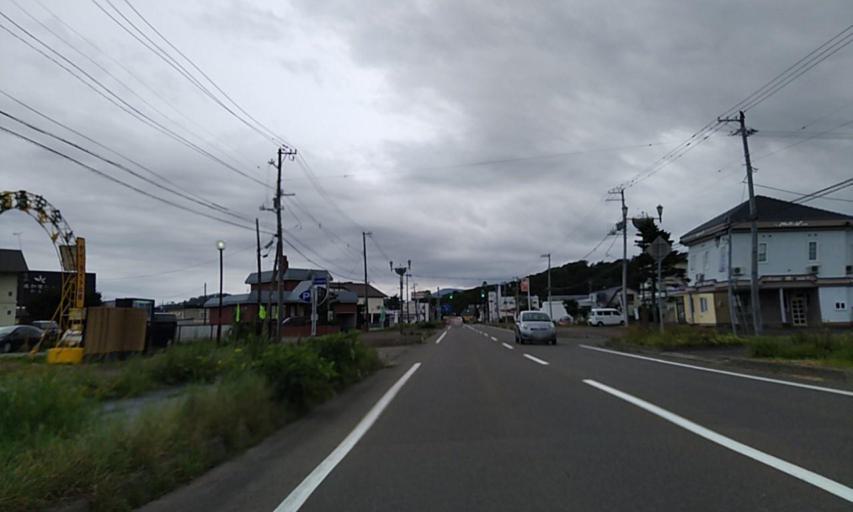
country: JP
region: Hokkaido
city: Obihiro
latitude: 42.2958
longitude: 143.3134
